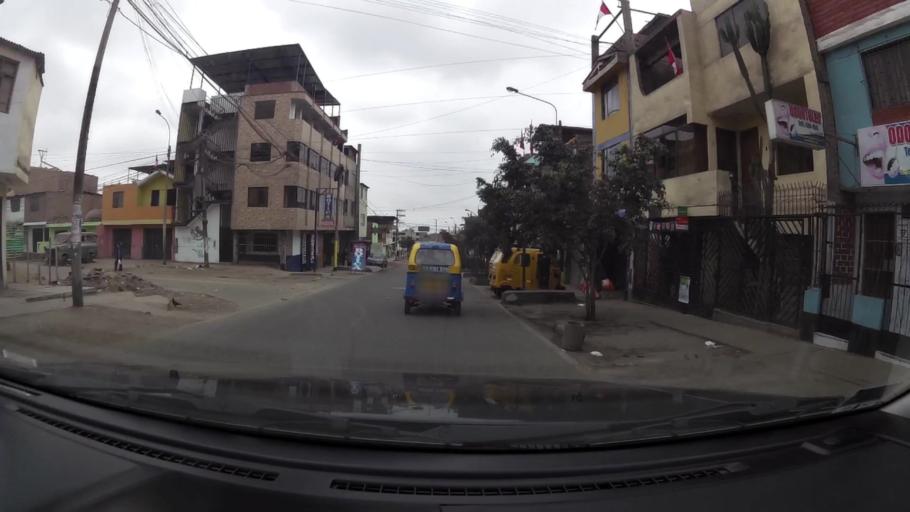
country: PE
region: Lima
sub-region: Lima
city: Surco
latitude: -12.1492
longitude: -76.9667
